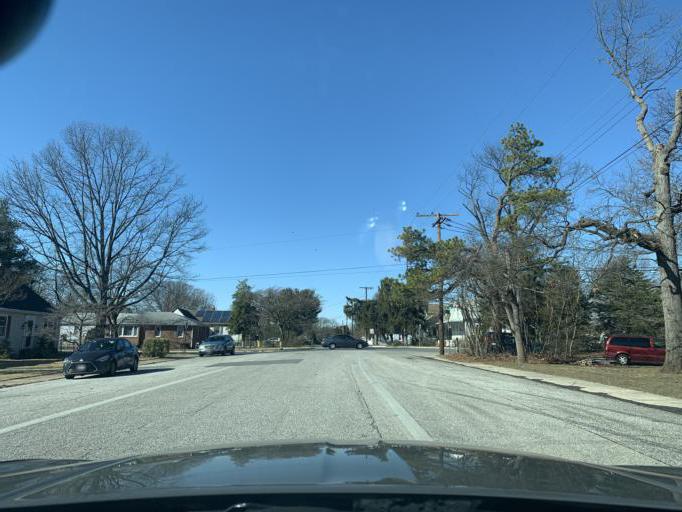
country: US
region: Maryland
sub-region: Anne Arundel County
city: Glen Burnie
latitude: 39.1628
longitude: -76.6327
